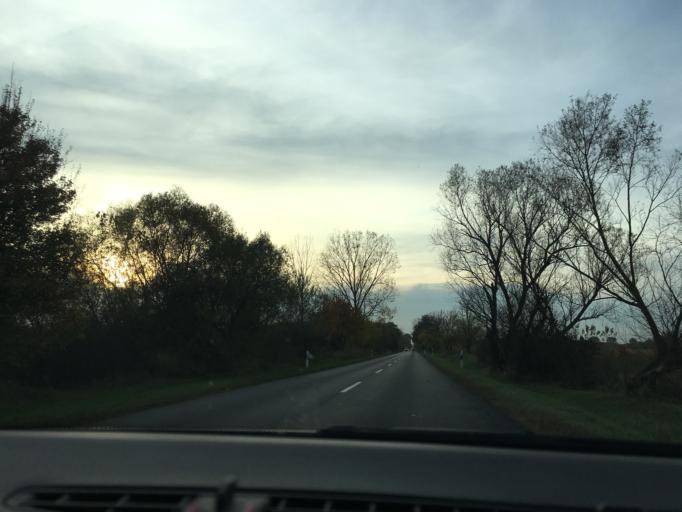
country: HU
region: Szabolcs-Szatmar-Bereg
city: Kisleta
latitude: 47.8546
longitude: 21.9963
